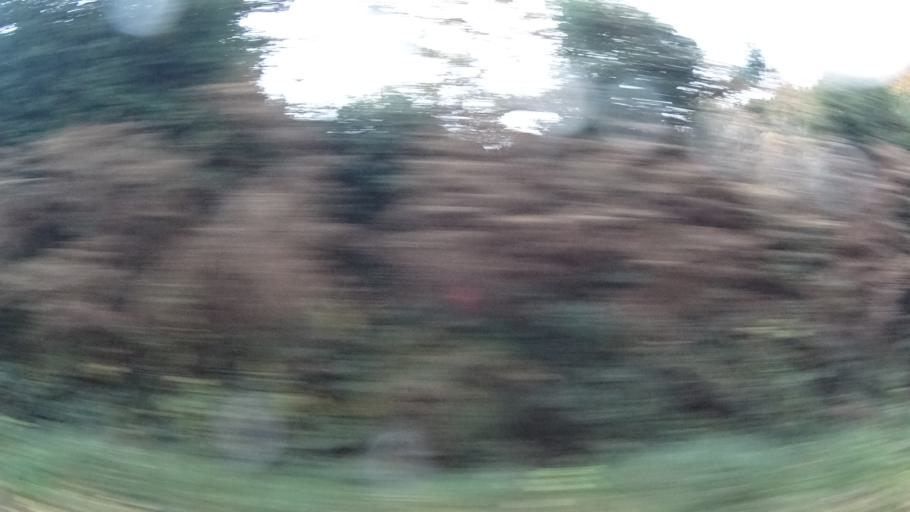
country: FR
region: Pays de la Loire
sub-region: Departement de la Loire-Atlantique
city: Avessac
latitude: 47.6631
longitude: -2.0115
